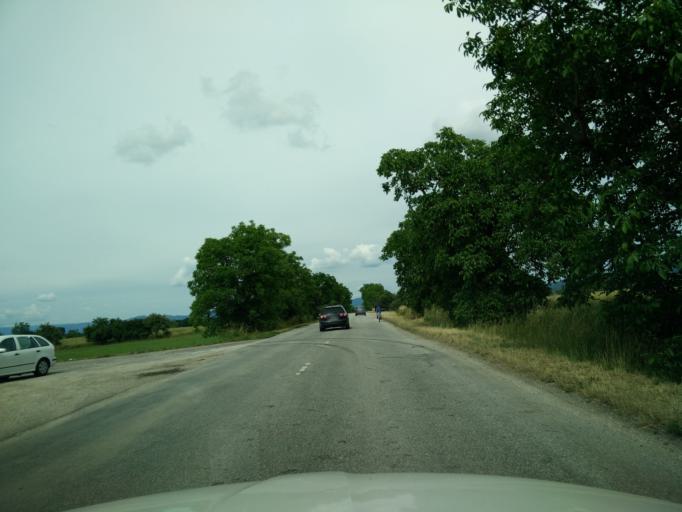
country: SK
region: Nitriansky
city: Novaky
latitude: 48.7279
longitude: 18.5563
